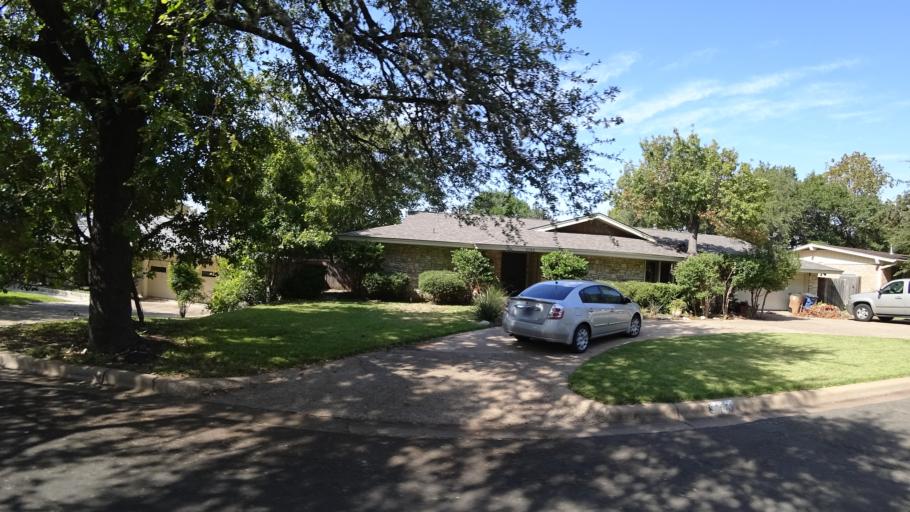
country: US
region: Texas
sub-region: Travis County
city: West Lake Hills
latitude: 30.3465
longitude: -97.7642
